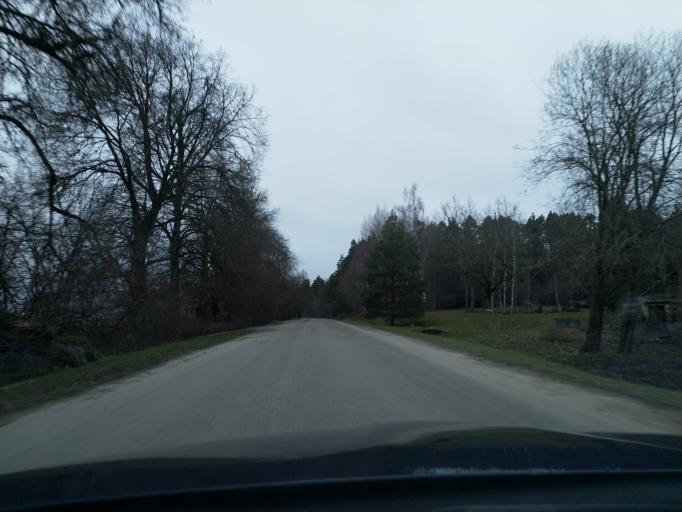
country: LV
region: Ventspils Rajons
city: Piltene
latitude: 57.1234
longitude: 21.8109
